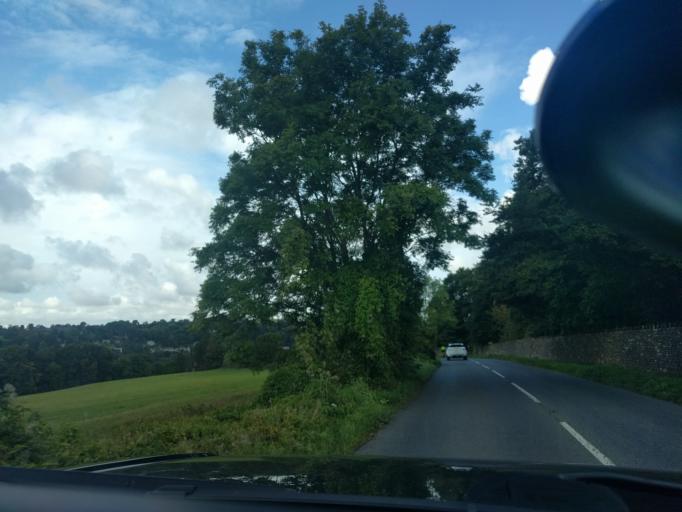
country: GB
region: England
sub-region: Bath and North East Somerset
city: Freshford
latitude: 51.3484
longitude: -2.3008
